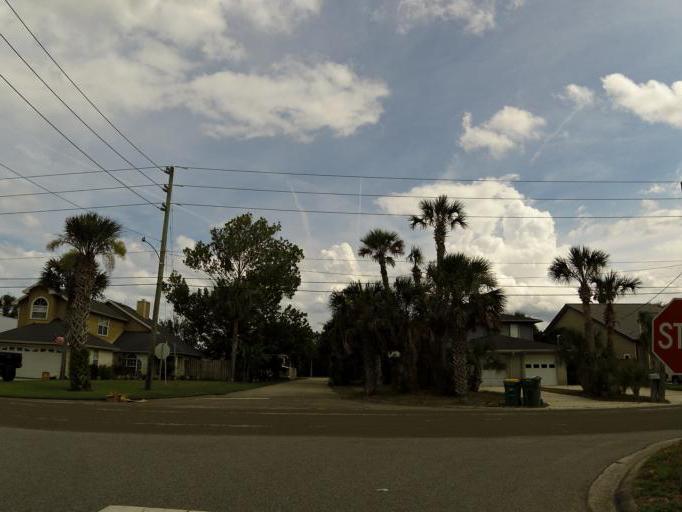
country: US
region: Florida
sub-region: Duval County
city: Jacksonville Beach
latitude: 30.2786
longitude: -81.3922
